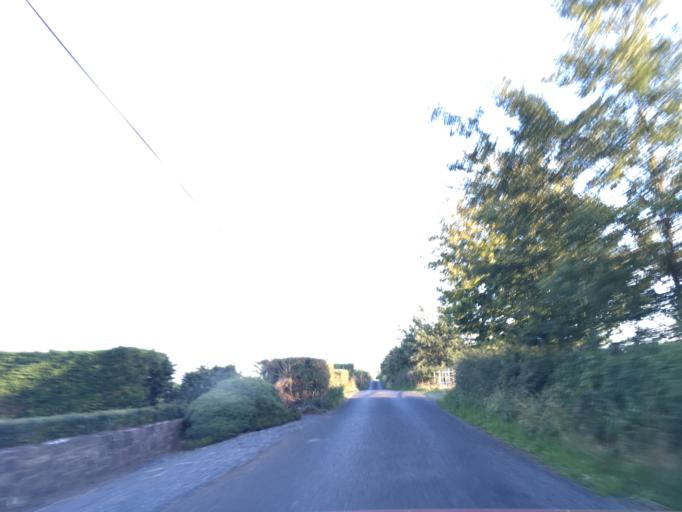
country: IE
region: Munster
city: Cashel
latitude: 52.5021
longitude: -7.9314
